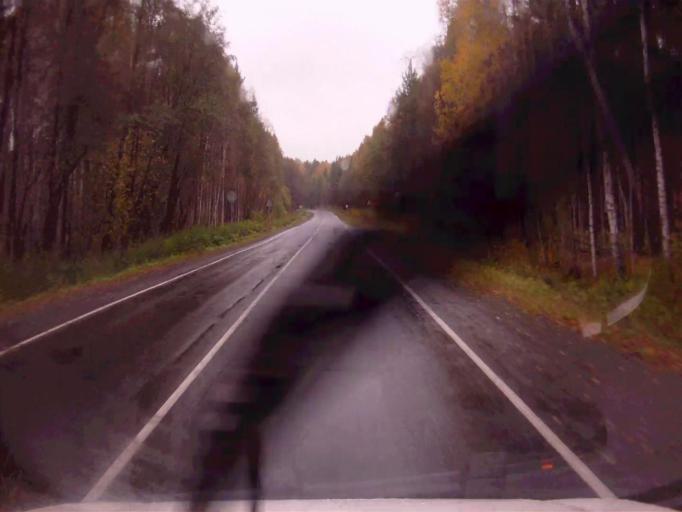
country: RU
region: Chelyabinsk
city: Verkhniy Ufaley
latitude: 55.9552
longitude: 60.3915
